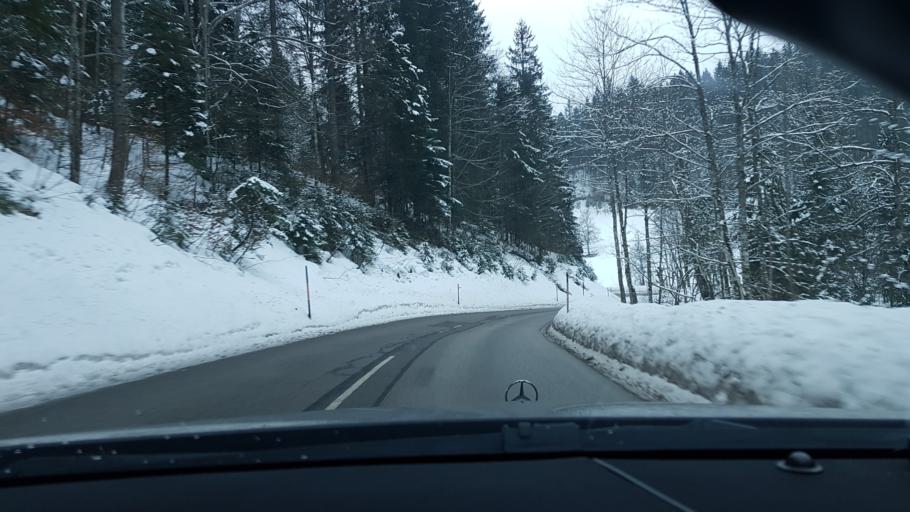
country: AT
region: Lower Austria
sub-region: Politischer Bezirk Scheibbs
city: Gaming
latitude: 47.8699
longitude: 15.1218
